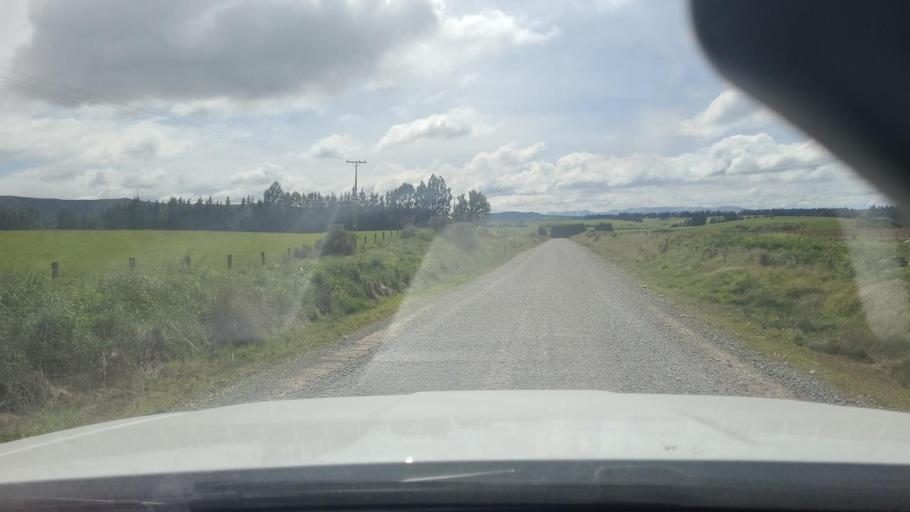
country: NZ
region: Southland
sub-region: Southland District
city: Te Anau
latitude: -45.4869
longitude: 167.8914
